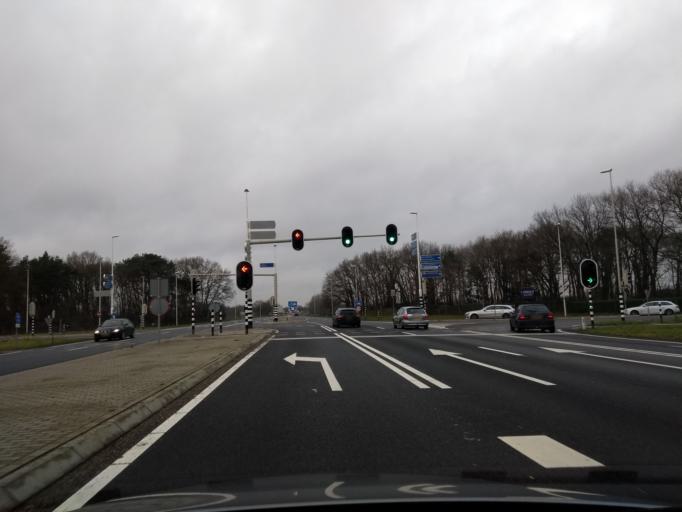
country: NL
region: Overijssel
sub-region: Gemeente Twenterand
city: Vroomshoop
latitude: 52.5096
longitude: 6.5633
